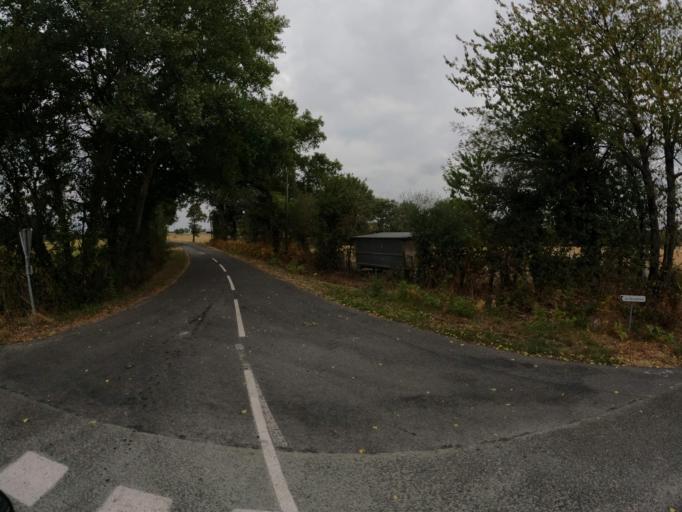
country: FR
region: Pays de la Loire
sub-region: Departement de Maine-et-Loire
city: Le Longeron
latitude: 47.0376
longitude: -1.0379
